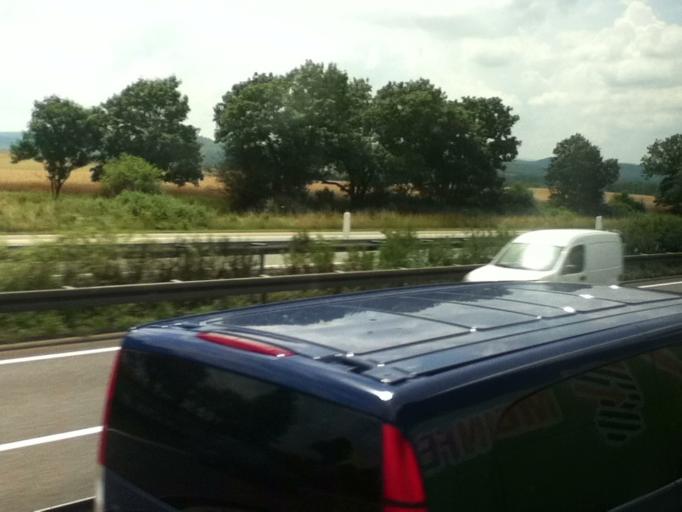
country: DE
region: Thuringia
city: Apfelstadt
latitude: 50.8940
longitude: 10.9066
